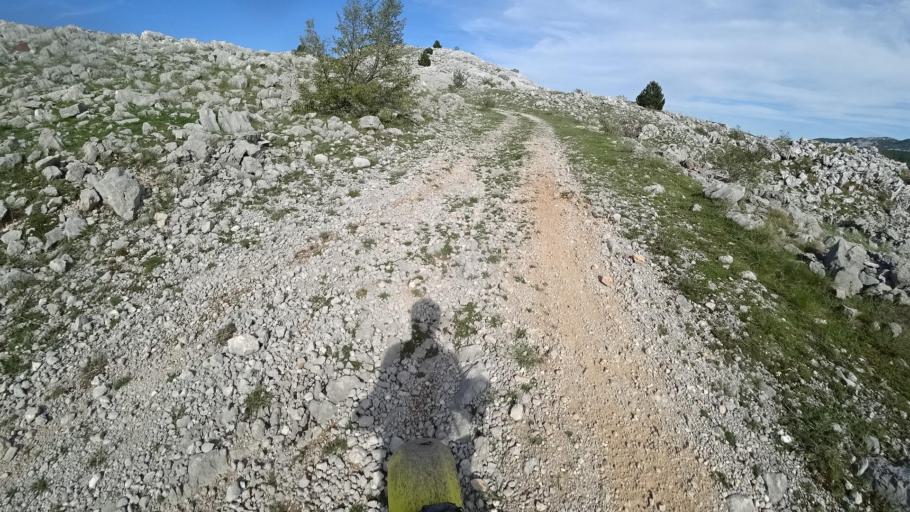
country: BA
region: Federation of Bosnia and Herzegovina
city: Kocerin
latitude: 43.5565
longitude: 17.4936
